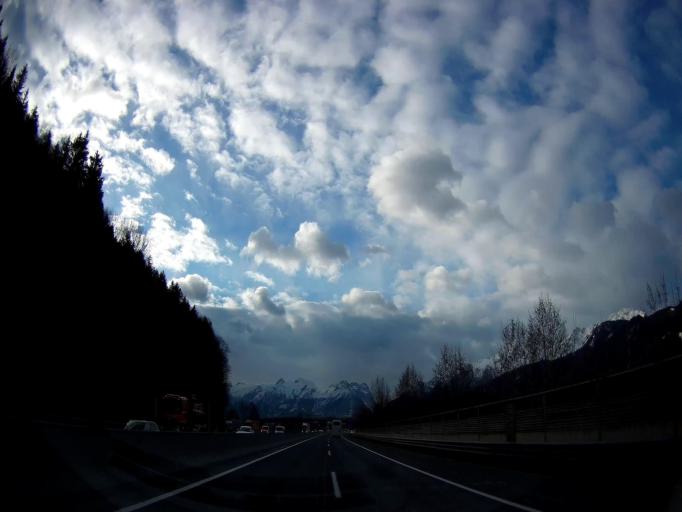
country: AT
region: Salzburg
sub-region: Politischer Bezirk Hallein
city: Adnet
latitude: 47.6802
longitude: 13.1219
